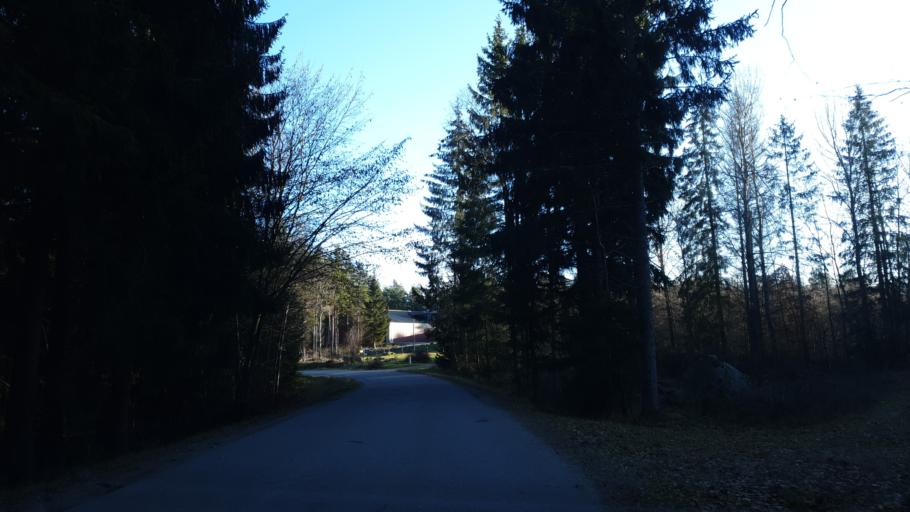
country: SE
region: Blekinge
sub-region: Ronneby Kommun
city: Brakne-Hoby
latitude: 56.2310
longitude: 15.1632
